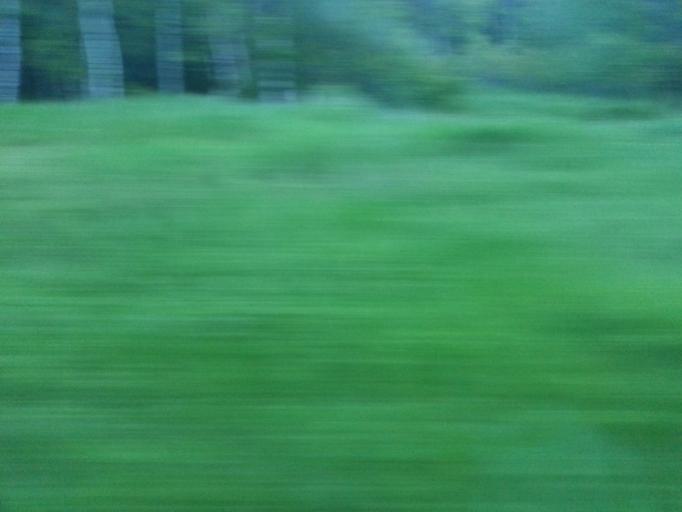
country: NO
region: Oppland
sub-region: Dovre
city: Dombas
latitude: 62.0567
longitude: 9.1344
